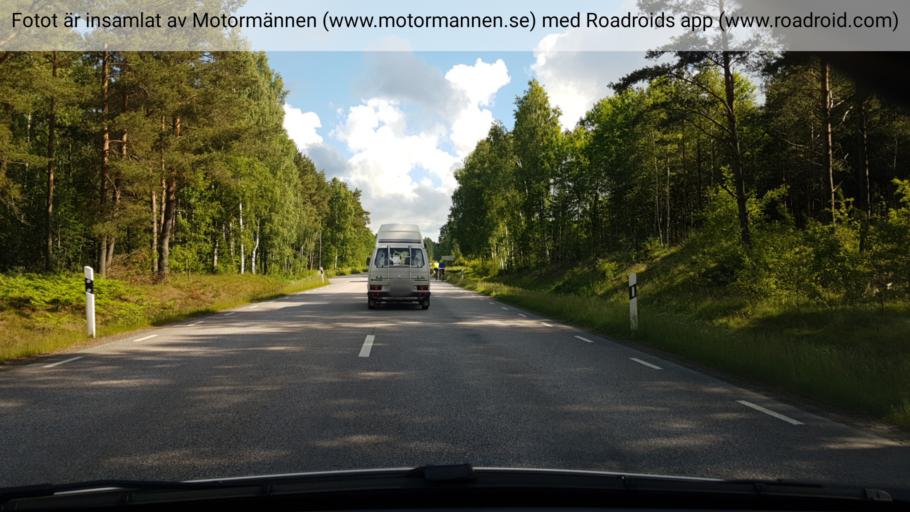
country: SE
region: Vaestra Goetaland
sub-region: Karlsborgs Kommun
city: Karlsborg
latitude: 58.5865
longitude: 14.5033
